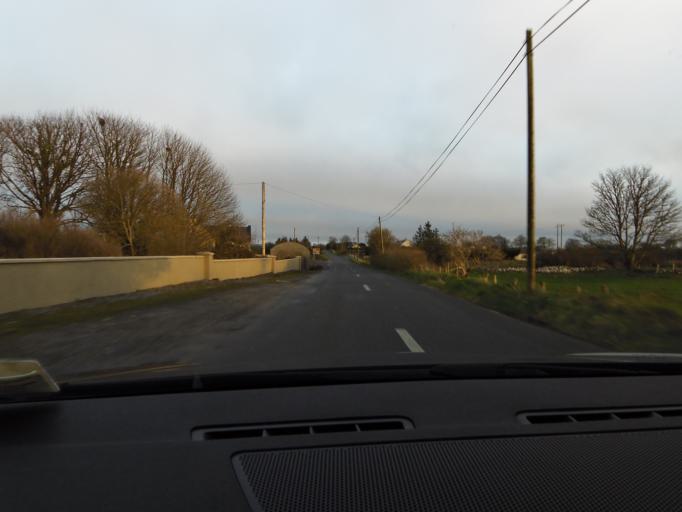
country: IE
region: Connaught
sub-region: Sligo
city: Ballymote
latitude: 54.0234
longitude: -8.5666
